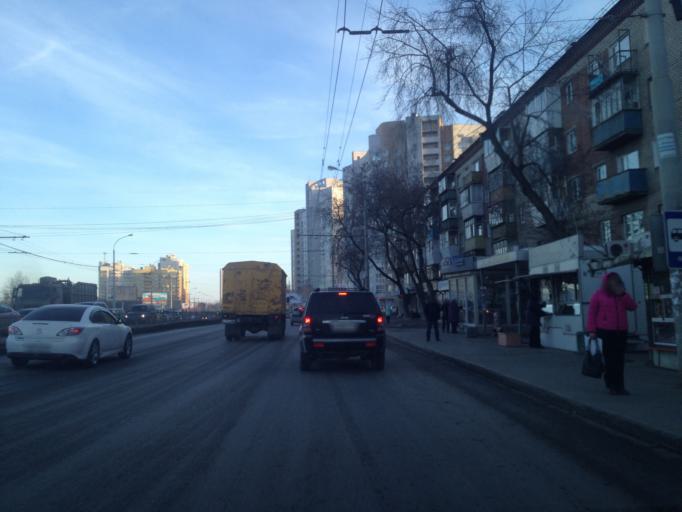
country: RU
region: Sverdlovsk
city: Yekaterinburg
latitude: 56.7870
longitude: 60.6480
